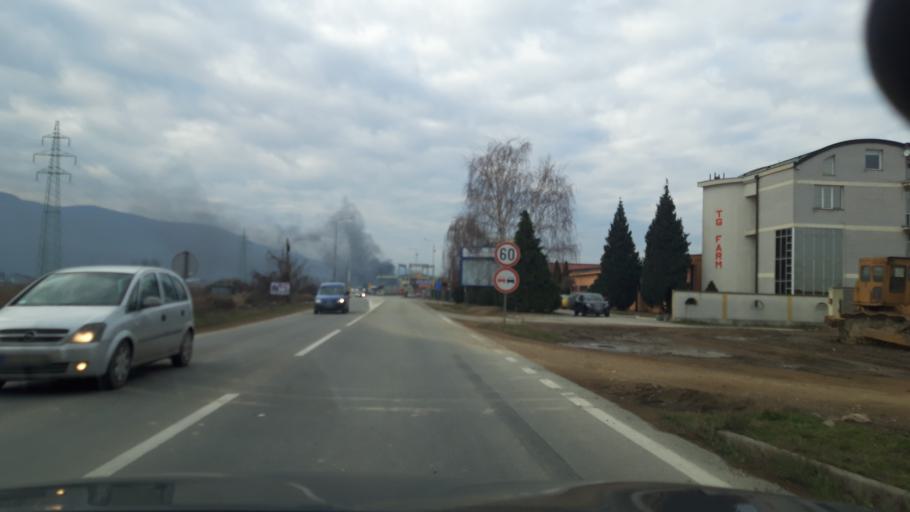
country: RS
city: Lipnicki Sor
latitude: 44.5419
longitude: 19.1877
